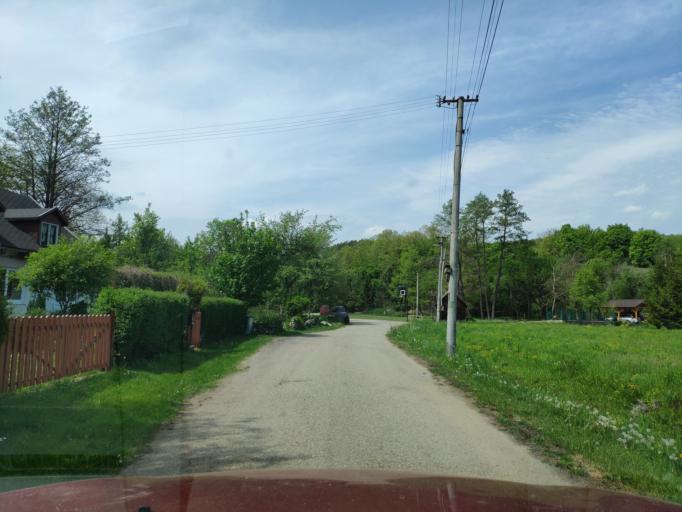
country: SK
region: Banskobystricky
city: Rimavska Sobota
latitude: 48.4837
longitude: 20.0705
